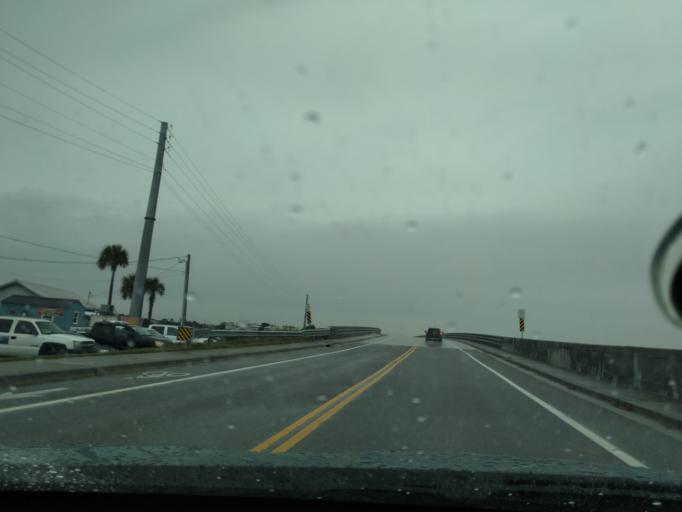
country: US
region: South Carolina
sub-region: Charleston County
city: Folly Beach
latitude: 32.6745
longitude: -79.9498
